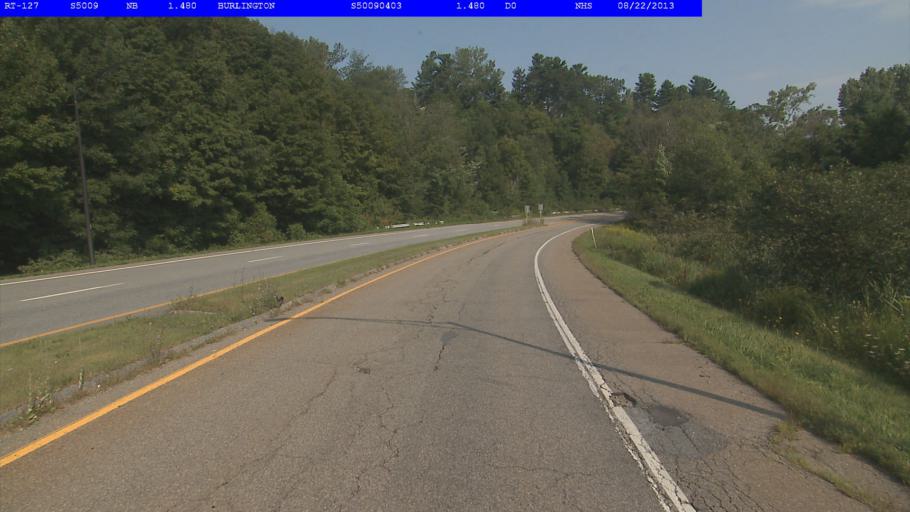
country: US
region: Vermont
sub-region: Chittenden County
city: Burlington
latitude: 44.5059
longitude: -73.2335
